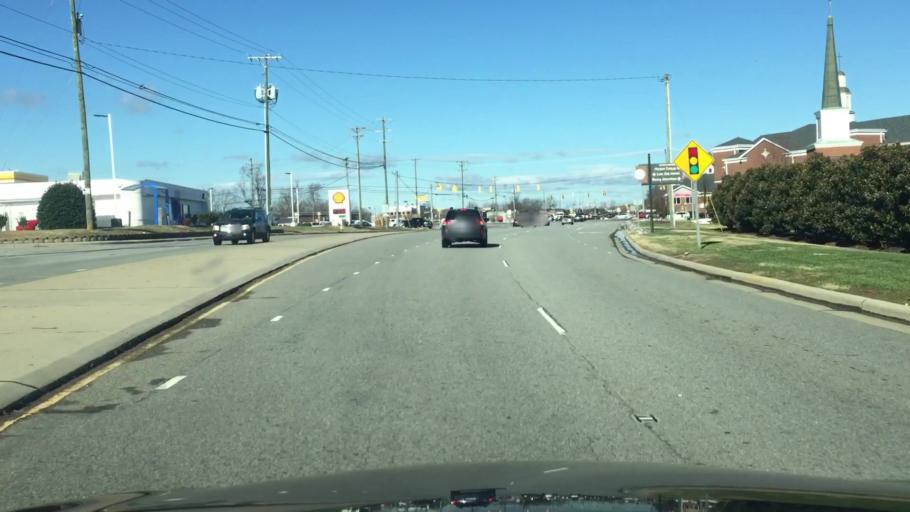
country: US
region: North Carolina
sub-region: Iredell County
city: Mooresville
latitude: 35.5824
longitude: -80.8734
